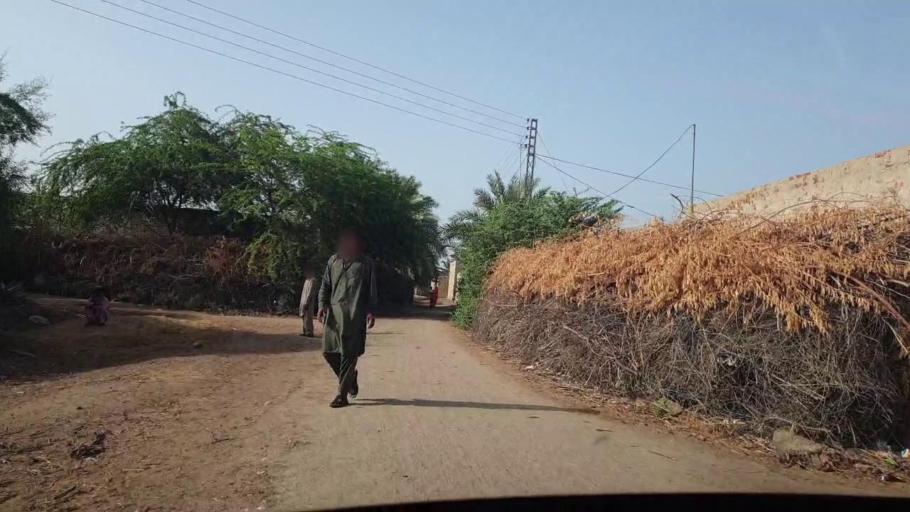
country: PK
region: Sindh
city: Nawabshah
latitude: 26.2425
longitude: 68.4499
